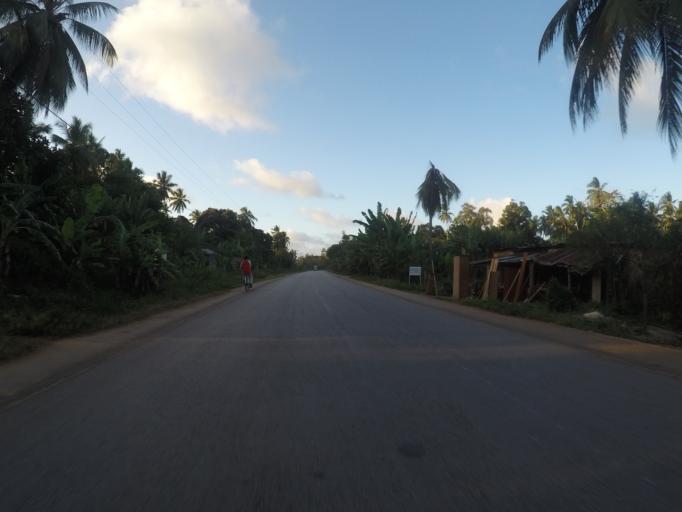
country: TZ
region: Zanzibar Central/South
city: Koani
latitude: -6.1322
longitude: 39.3253
